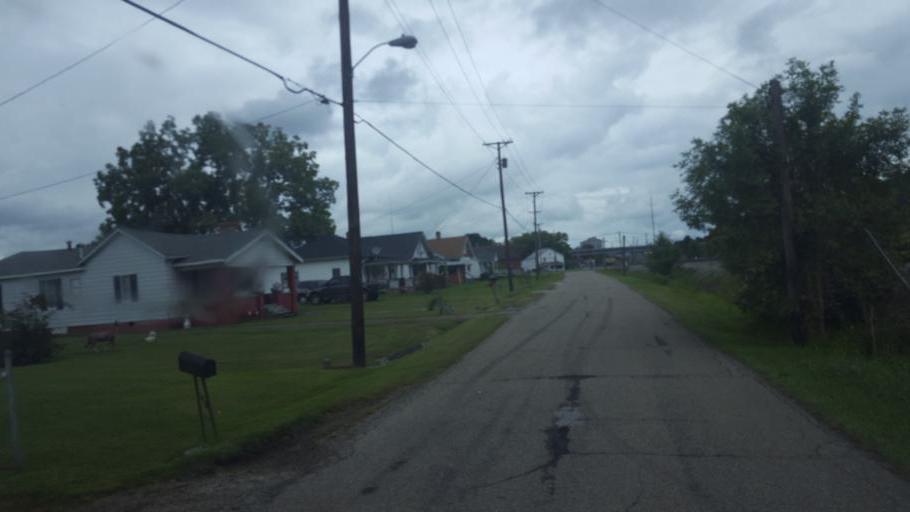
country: US
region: Kentucky
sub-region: Greenup County
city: South Shore
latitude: 38.7209
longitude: -82.9674
